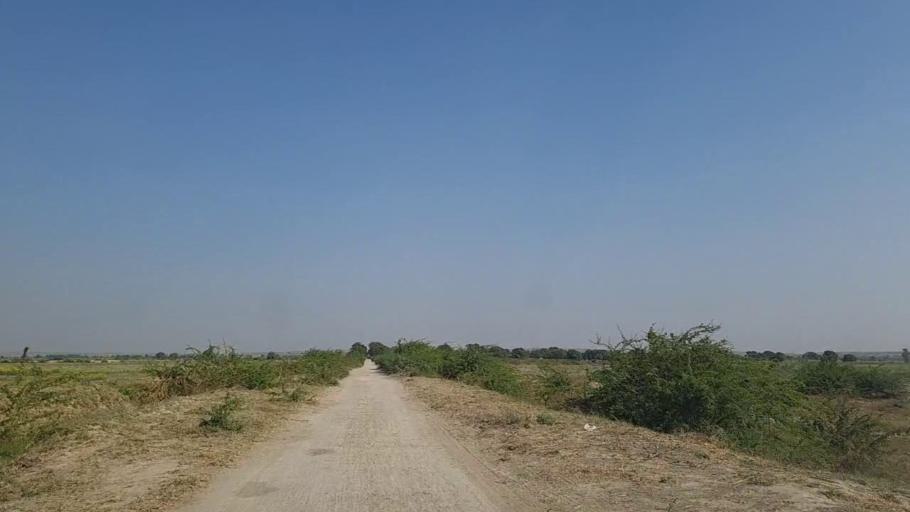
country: PK
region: Sindh
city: Naukot
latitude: 24.8990
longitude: 69.4838
